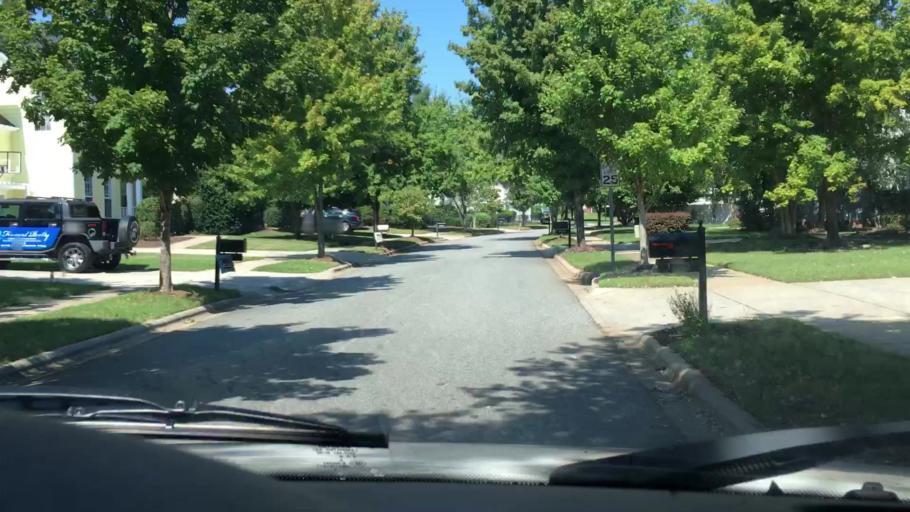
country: US
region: North Carolina
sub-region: Mecklenburg County
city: Cornelius
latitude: 35.4515
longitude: -80.8811
